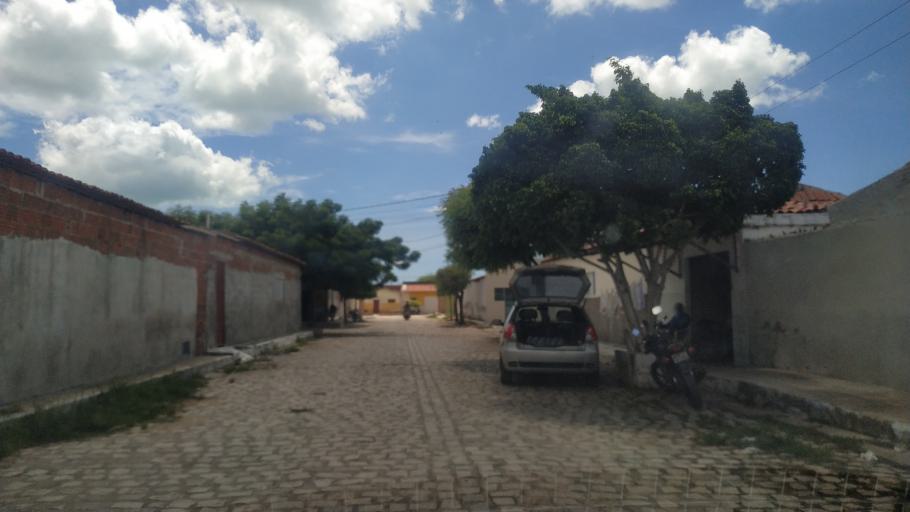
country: BR
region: Rio Grande do Norte
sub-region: Areia Branca
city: Areia Branca
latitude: -4.9489
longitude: -37.1266
